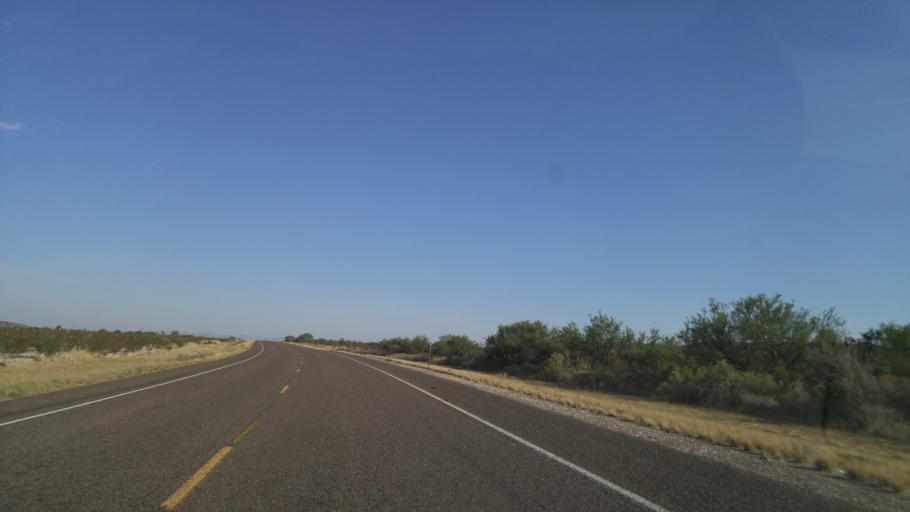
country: US
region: Texas
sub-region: Brewster County
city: Alpine
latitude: 29.7572
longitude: -103.5706
